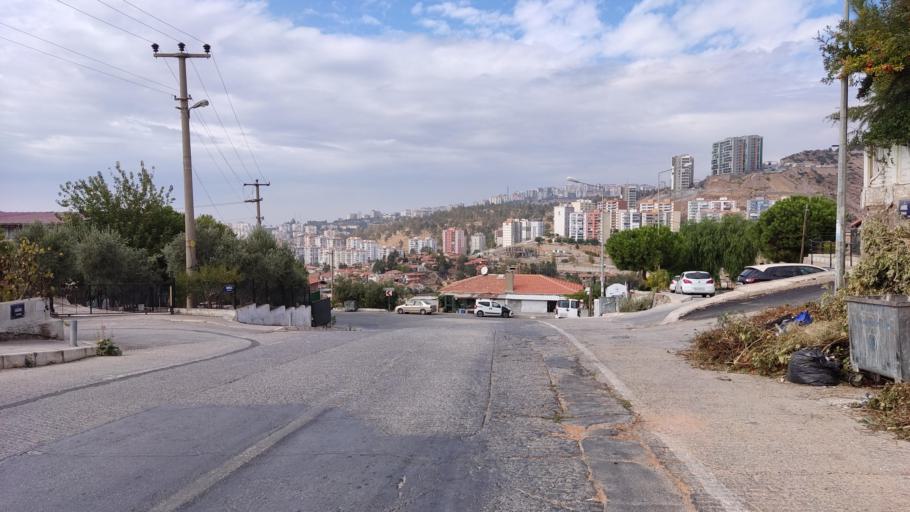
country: TR
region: Izmir
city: Karsiyaka
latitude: 38.5008
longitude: 27.0855
